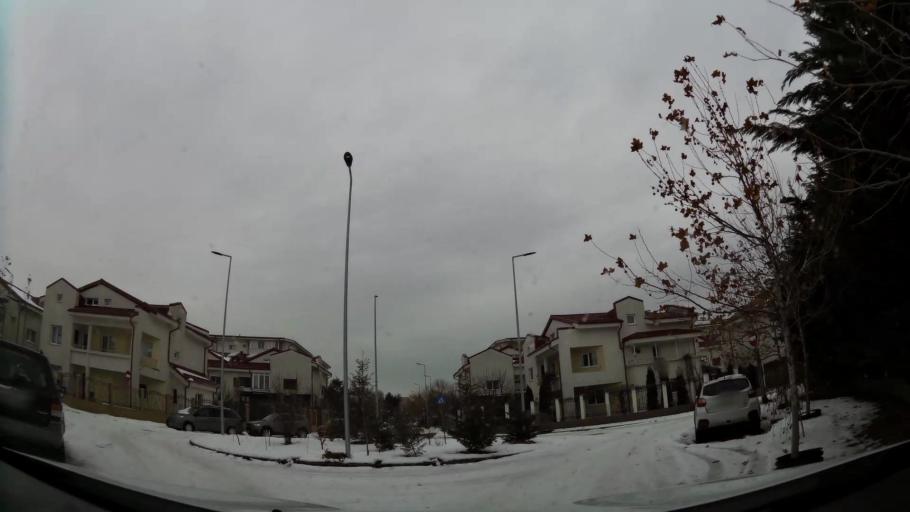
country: RO
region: Bucuresti
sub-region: Municipiul Bucuresti
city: Bucuresti
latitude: 44.4103
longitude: 26.0523
